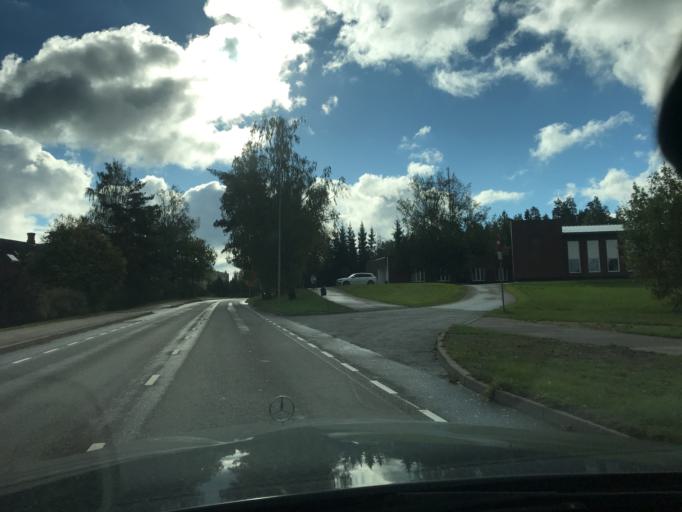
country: EE
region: Valgamaa
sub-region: Torva linn
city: Torva
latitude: 57.9967
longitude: 25.9350
